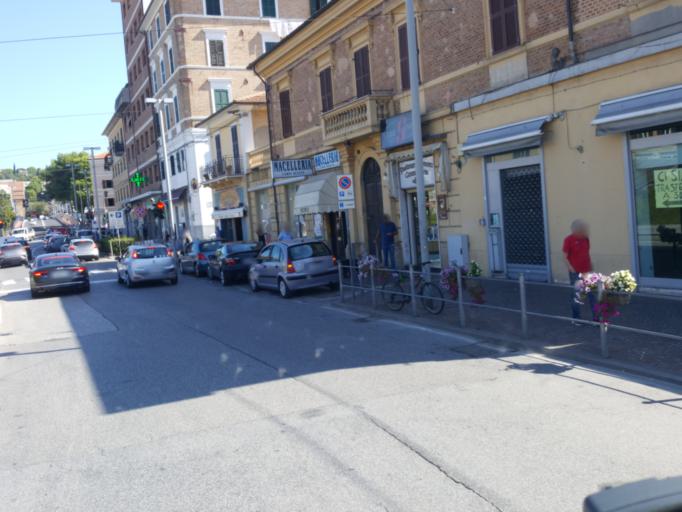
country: IT
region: The Marches
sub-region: Provincia di Ancona
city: Le Grazie di Ancona
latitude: 43.6031
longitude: 13.5075
